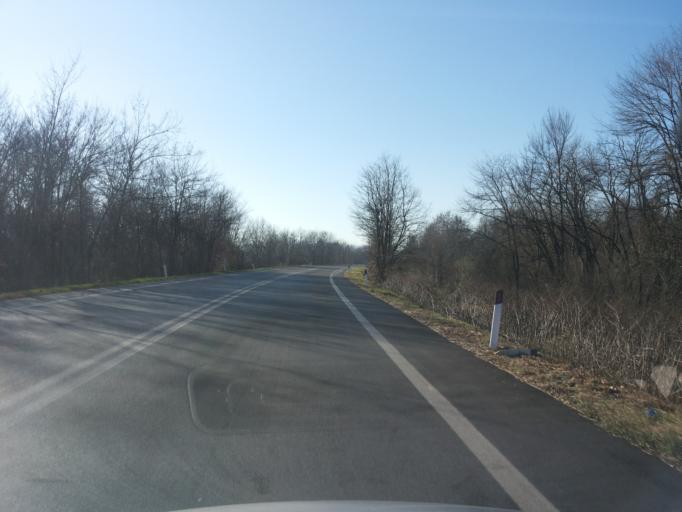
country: IT
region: Piedmont
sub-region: Provincia di Biella
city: Verrone
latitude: 45.4931
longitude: 8.1242
